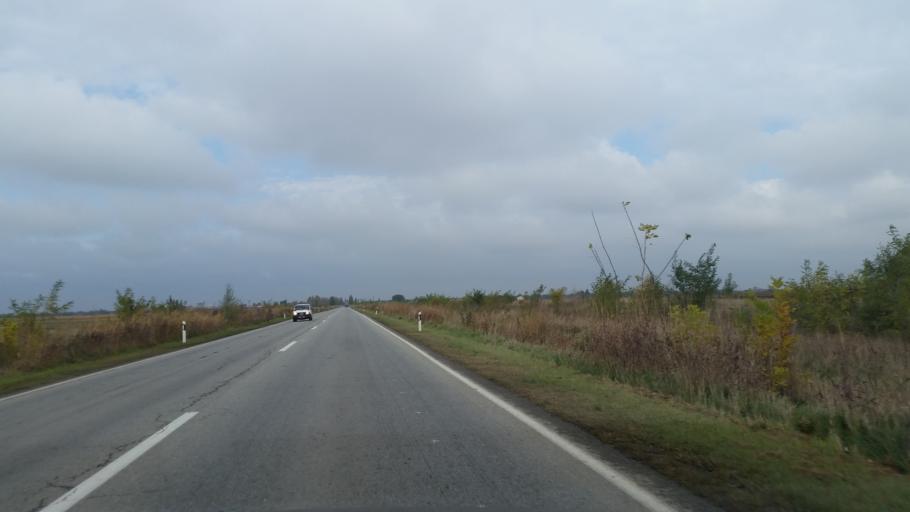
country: RS
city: Melenci
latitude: 45.4943
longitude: 20.3280
